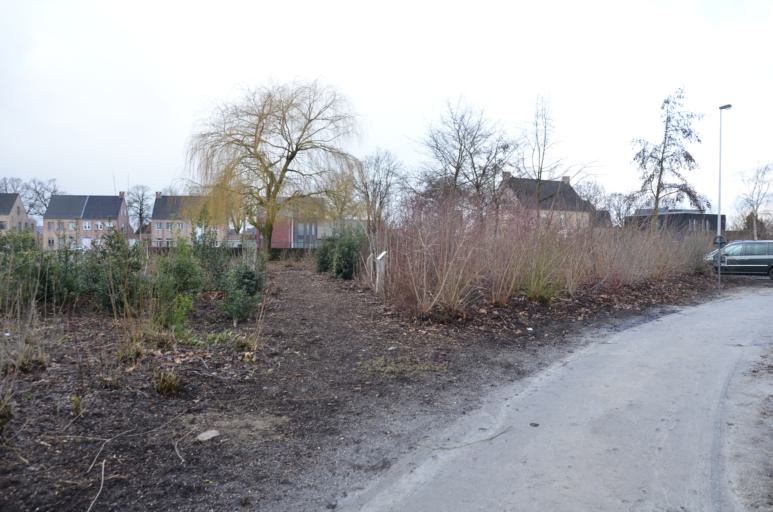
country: BE
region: Flanders
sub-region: Provincie Antwerpen
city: Brecht
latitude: 51.3944
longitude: 4.6467
